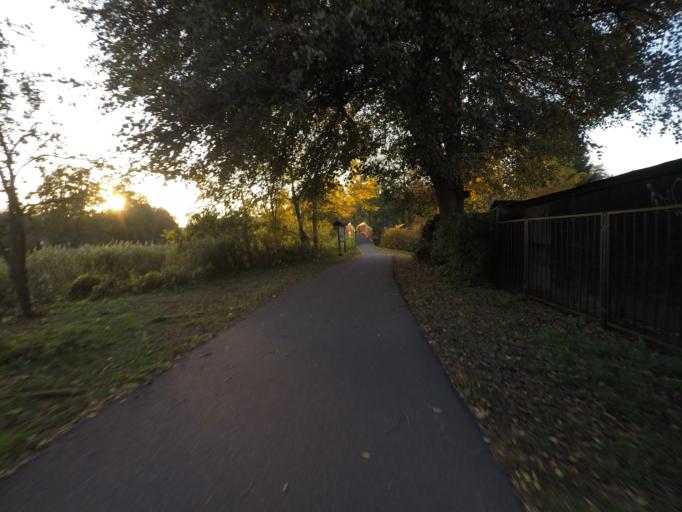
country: DE
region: Brandenburg
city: Melchow
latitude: 52.8460
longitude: 13.7153
